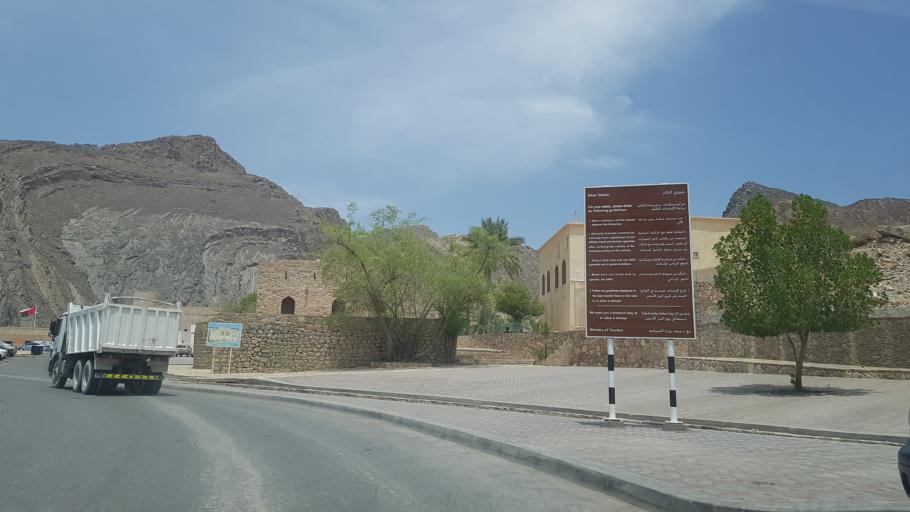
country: OM
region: Muhafazat ad Dakhiliyah
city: Izki
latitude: 22.9232
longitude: 57.6672
